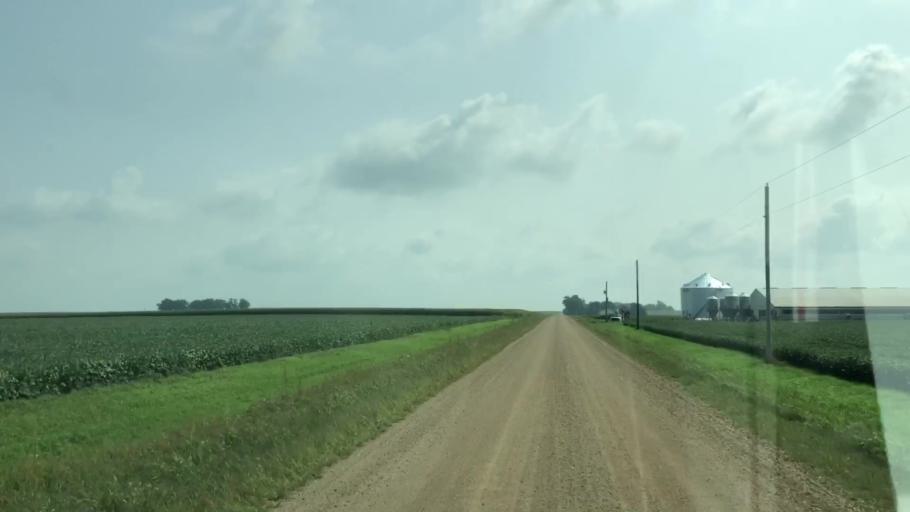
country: US
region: Iowa
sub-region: O'Brien County
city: Sheldon
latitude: 43.2153
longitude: -95.9545
